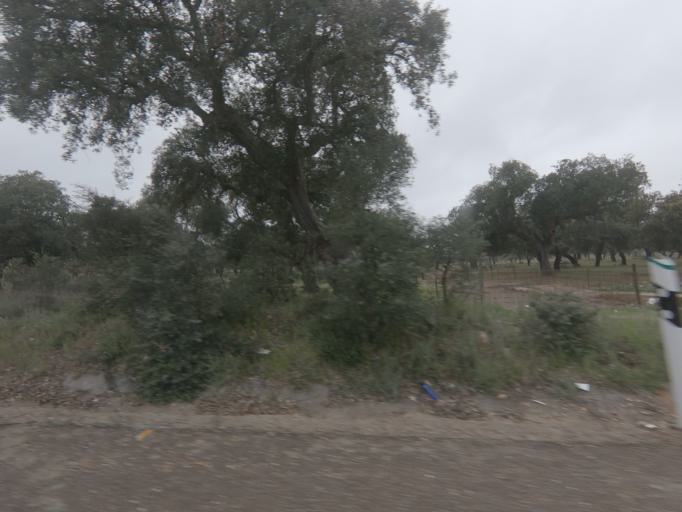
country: ES
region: Extremadura
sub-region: Provincia de Badajoz
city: Puebla de Obando
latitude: 39.1947
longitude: -6.5950
